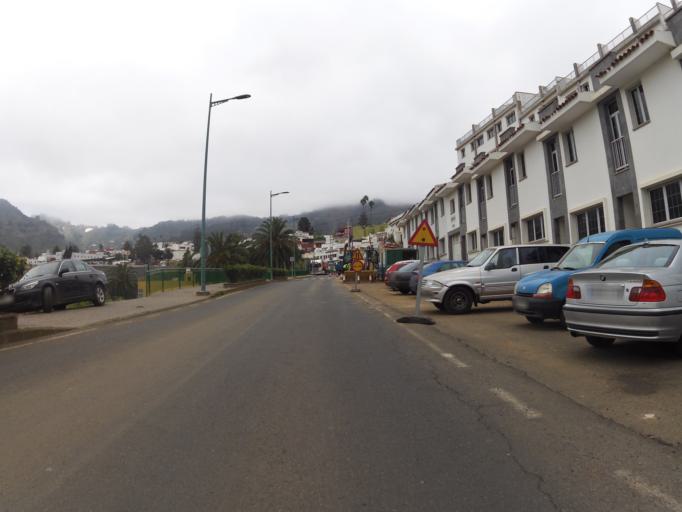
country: ES
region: Canary Islands
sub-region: Provincia de Las Palmas
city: Teror
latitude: 28.0618
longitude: -15.5421
